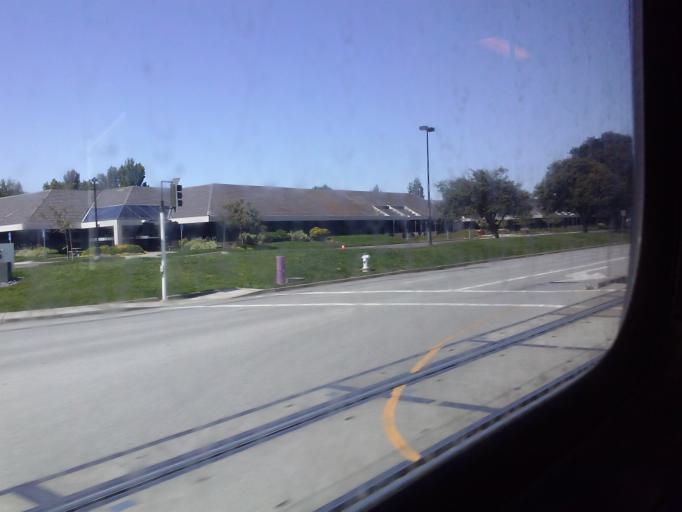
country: US
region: California
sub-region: Santa Clara County
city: Sunnyvale
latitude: 37.4115
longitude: -122.0180
